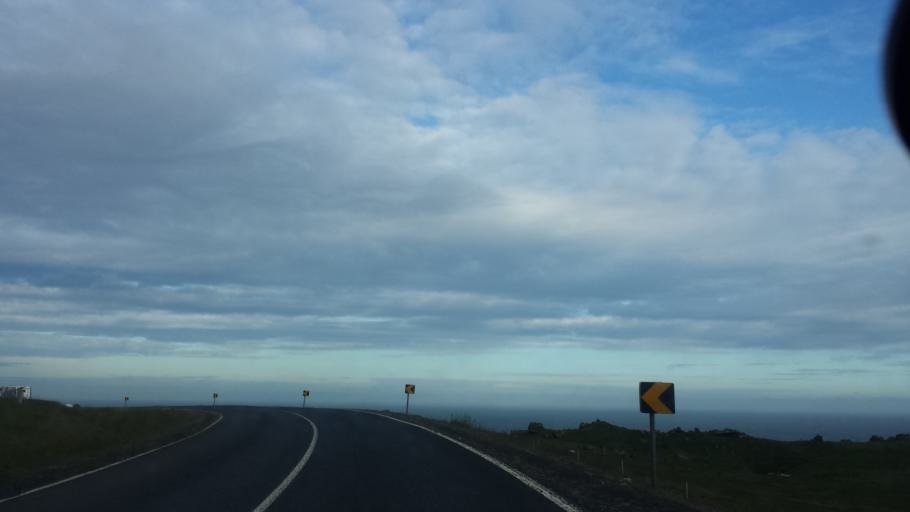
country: IS
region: South
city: Vestmannaeyjar
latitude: 63.4251
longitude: -20.2668
